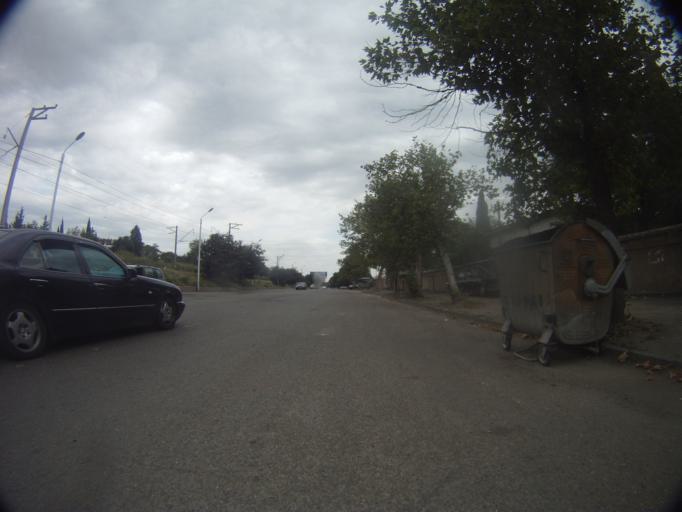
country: GE
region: T'bilisi
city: Tbilisi
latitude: 41.6845
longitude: 44.8882
